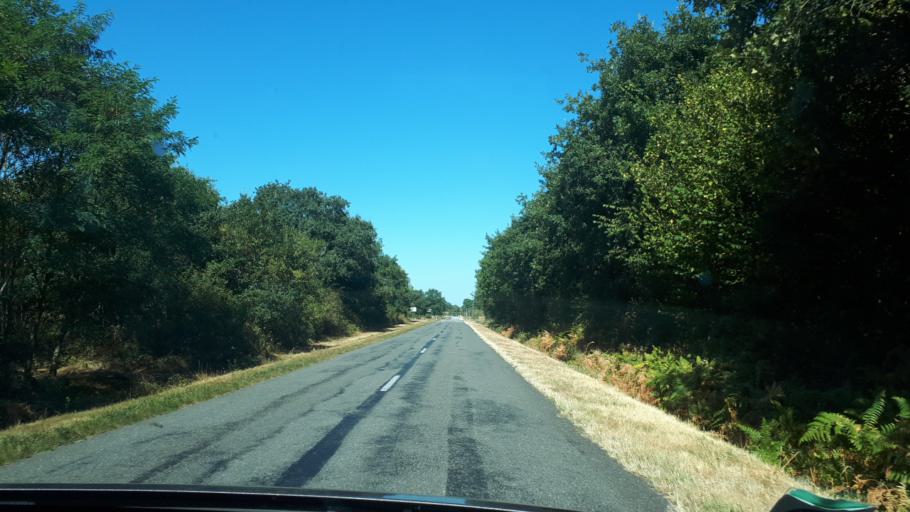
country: FR
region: Centre
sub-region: Departement du Loiret
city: Coullons
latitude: 47.6360
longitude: 2.4510
